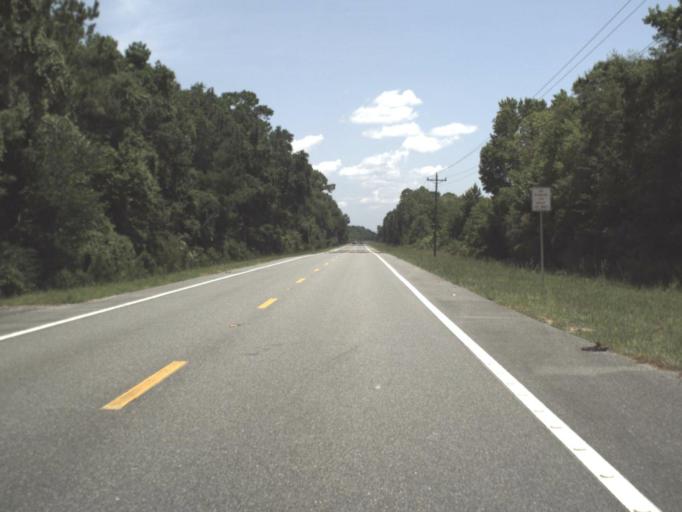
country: US
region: Florida
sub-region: Taylor County
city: Steinhatchee
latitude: 29.7337
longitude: -83.3590
